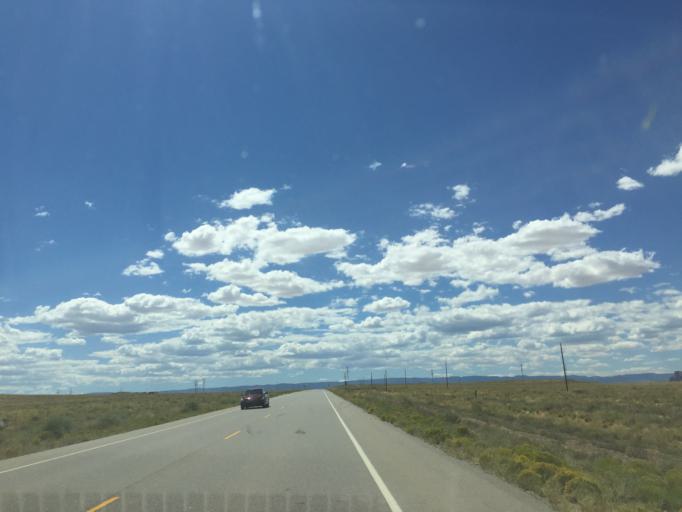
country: US
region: New Mexico
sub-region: San Juan County
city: Waterflow
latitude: 36.3581
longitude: -108.6048
